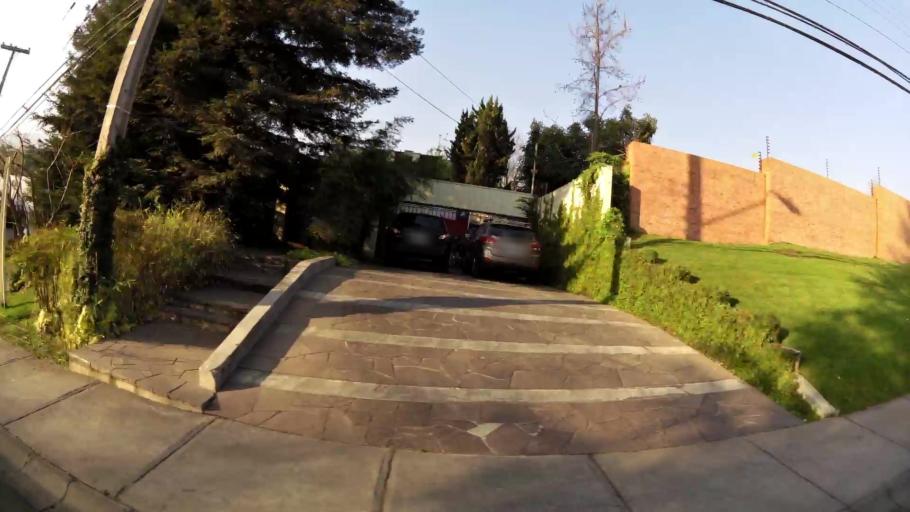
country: CL
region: Santiago Metropolitan
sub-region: Provincia de Santiago
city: Villa Presidente Frei, Nunoa, Santiago, Chile
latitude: -33.3388
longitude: -70.5107
